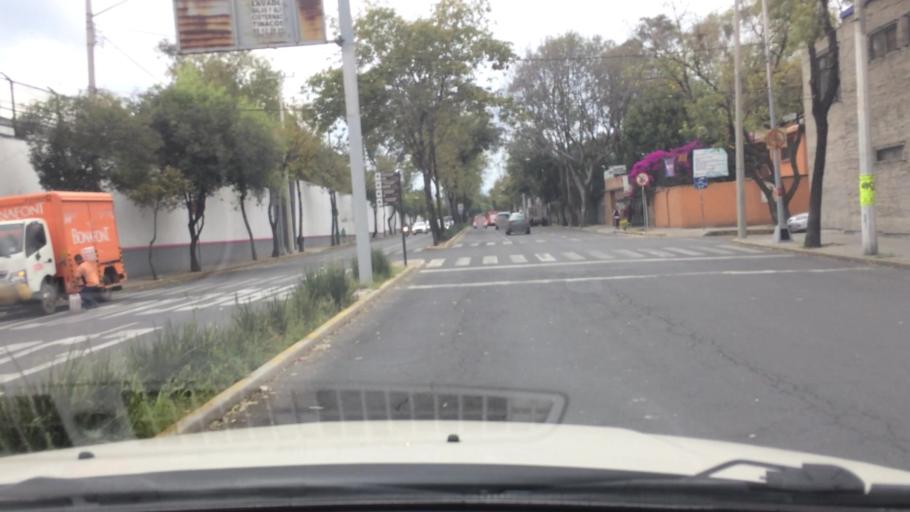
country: MX
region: Mexico City
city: Tlalpan
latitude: 19.2924
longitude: -99.1677
